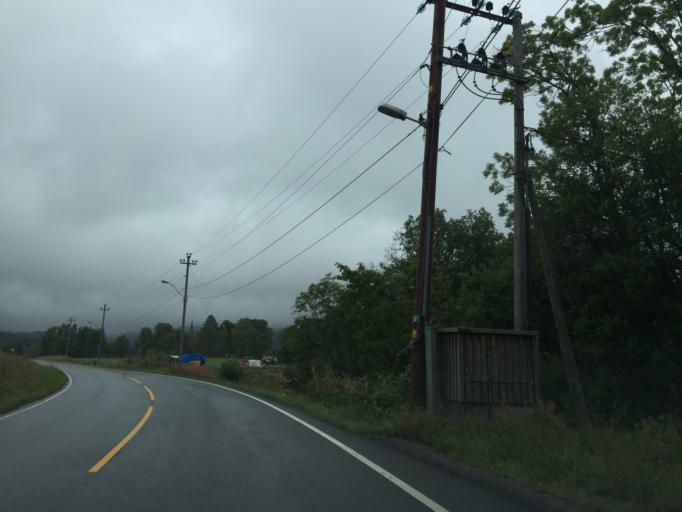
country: NO
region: Akershus
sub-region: Baerum
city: Lysaker
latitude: 60.0121
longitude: 10.6165
